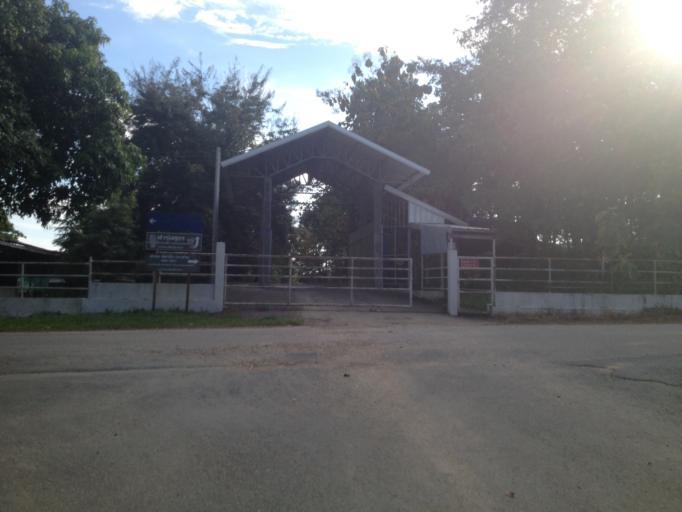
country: TH
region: Chiang Mai
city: Chiang Mai
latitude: 18.7570
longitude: 98.9393
